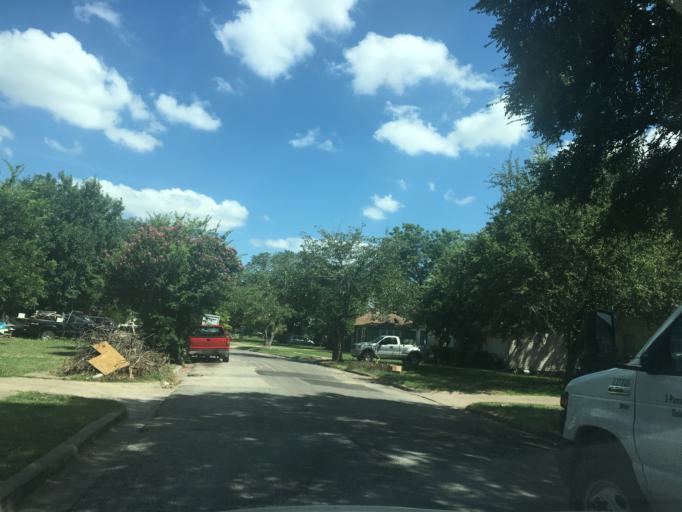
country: US
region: Texas
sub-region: Dallas County
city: Garland
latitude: 32.8415
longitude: -96.6918
